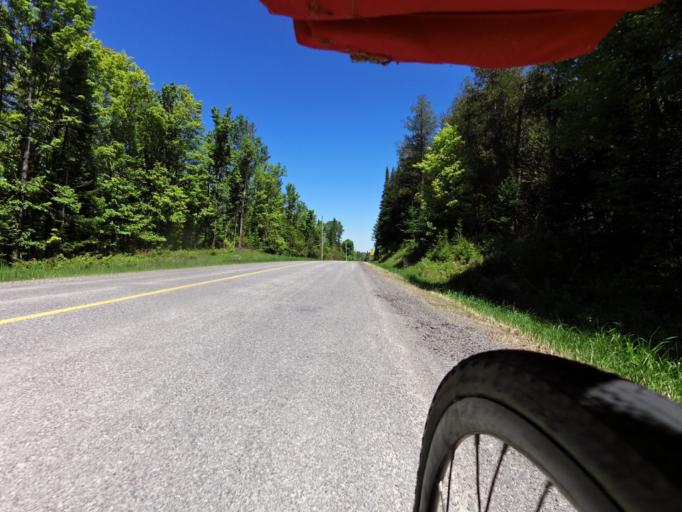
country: CA
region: Ontario
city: Carleton Place
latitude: 45.1748
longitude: -76.4089
